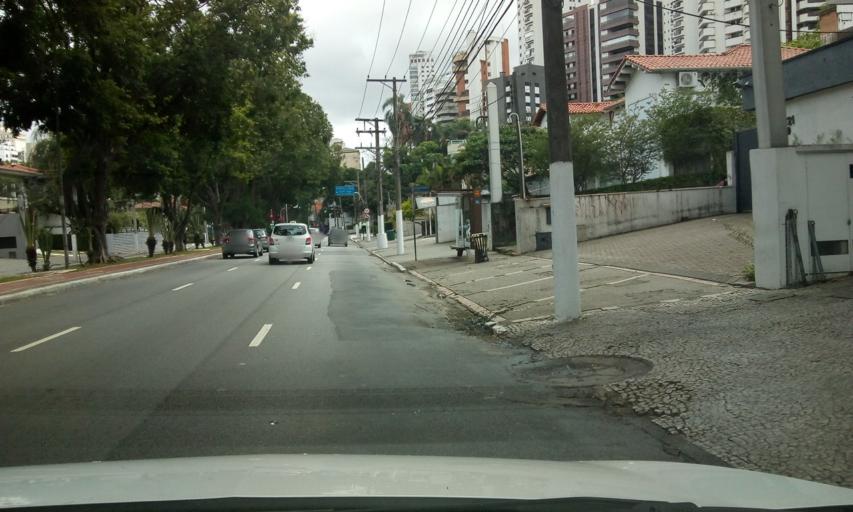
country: BR
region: Sao Paulo
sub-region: Sao Paulo
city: Sao Paulo
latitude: -23.5413
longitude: -46.6646
